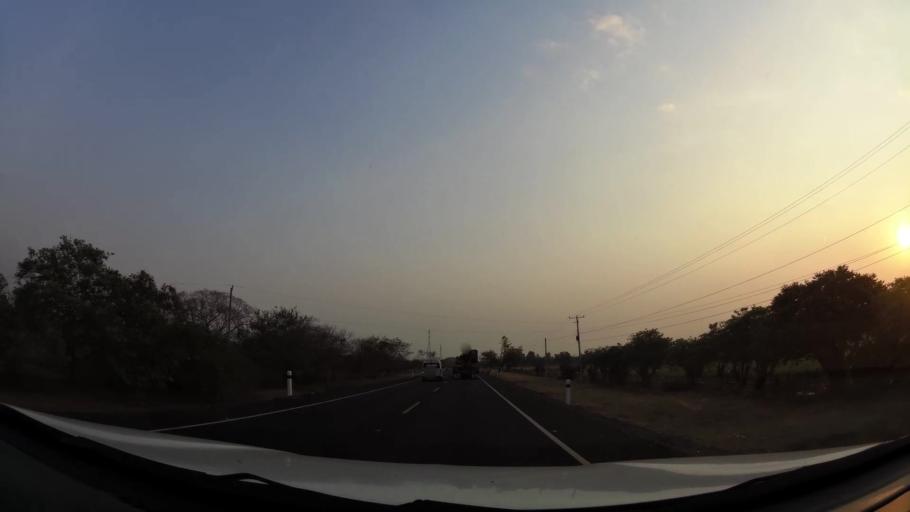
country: NI
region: Leon
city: La Paz Centro
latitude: 12.3242
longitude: -86.6896
